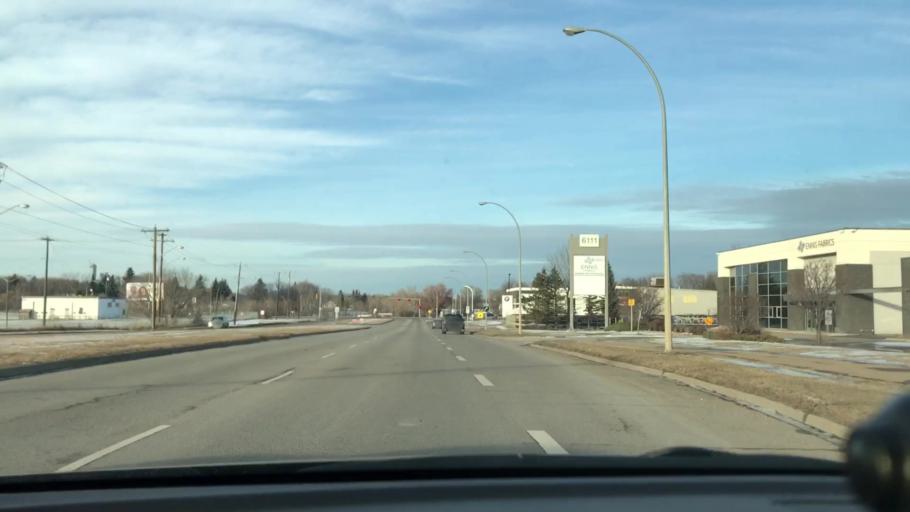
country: CA
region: Alberta
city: Edmonton
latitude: 53.4975
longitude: -113.4670
